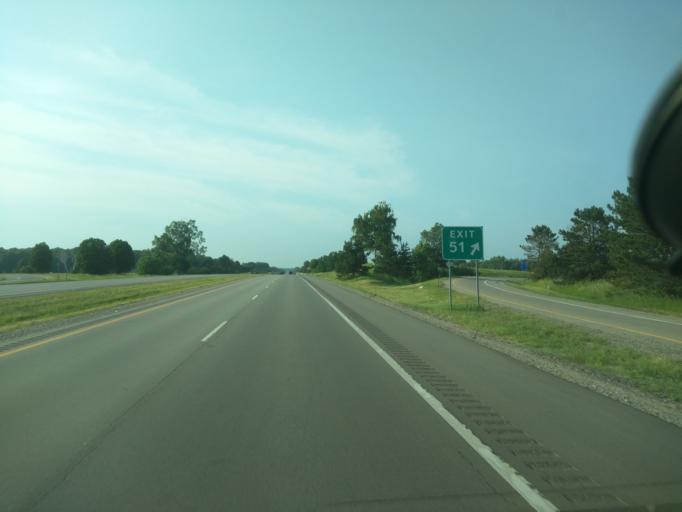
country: US
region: Michigan
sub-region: Ingham County
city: Leslie
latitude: 42.3750
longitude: -84.4289
